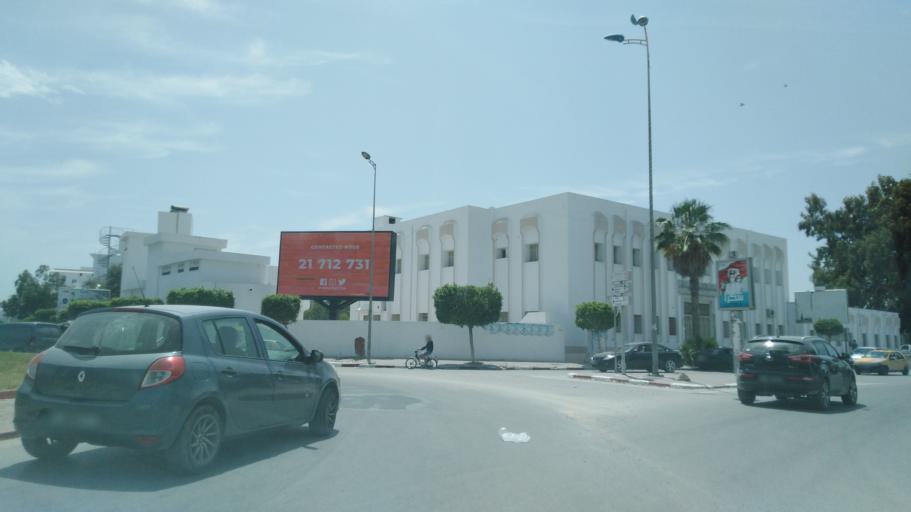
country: TN
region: Safaqis
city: Sfax
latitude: 34.7414
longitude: 10.7524
